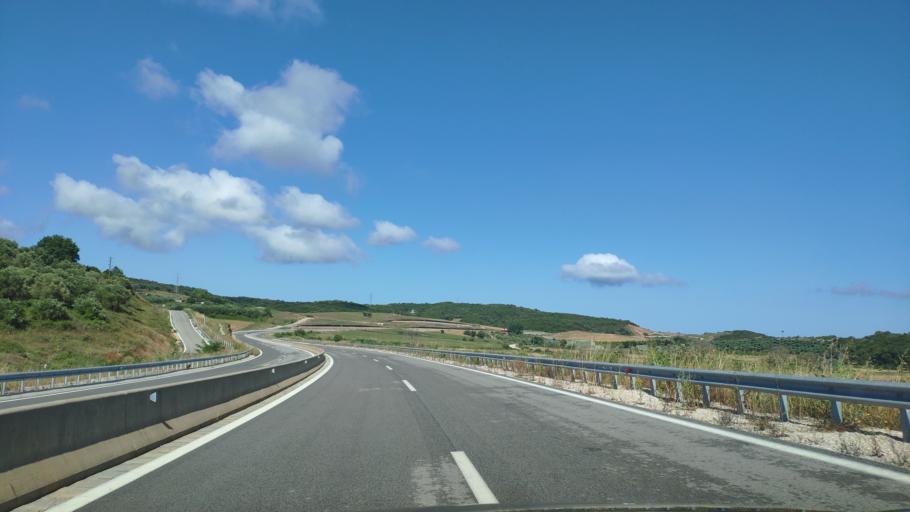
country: GR
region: West Greece
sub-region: Nomos Aitolias kai Akarnanias
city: Vonitsa
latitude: 38.9115
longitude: 20.8406
